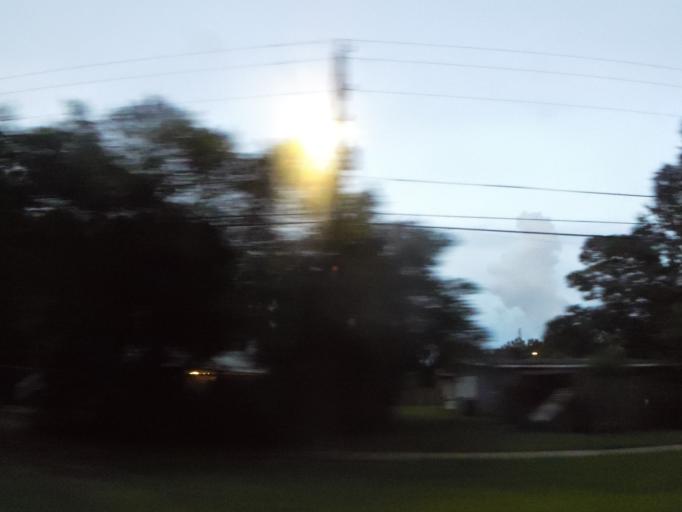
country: US
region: Florida
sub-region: Duval County
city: Jacksonville
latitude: 30.3685
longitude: -81.6085
